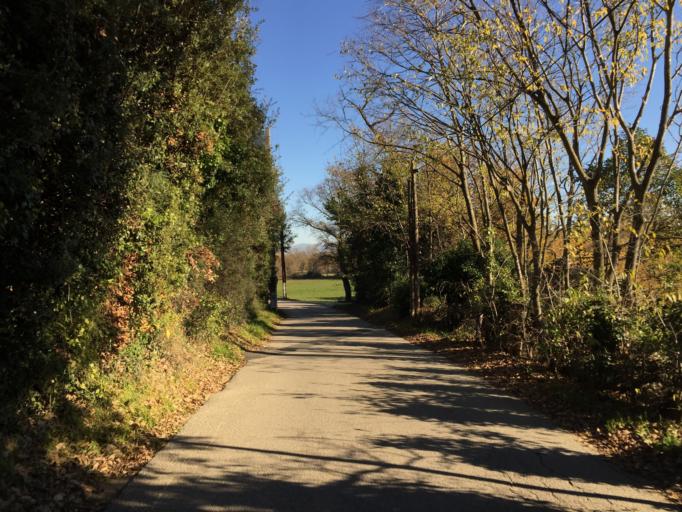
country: FR
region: Provence-Alpes-Cote d'Azur
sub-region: Departement du Vaucluse
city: Entraigues-sur-la-Sorgue
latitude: 44.0095
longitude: 4.9056
